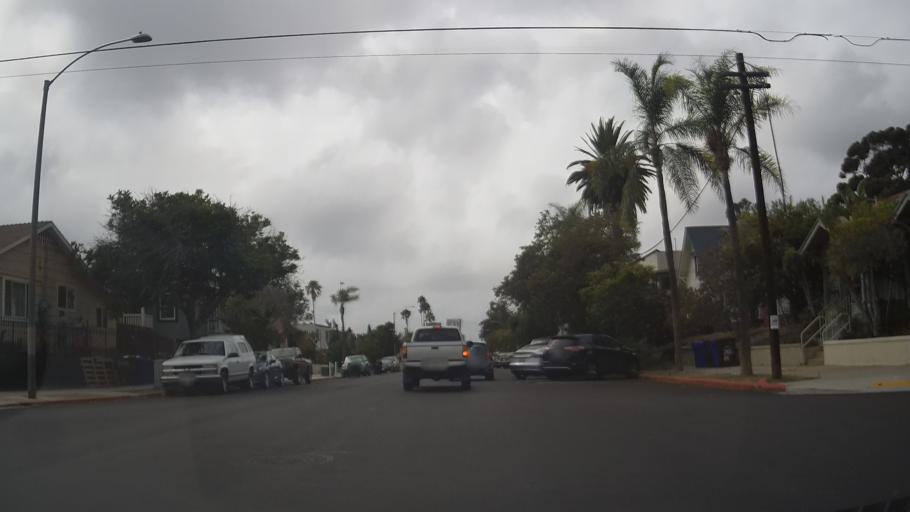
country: US
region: California
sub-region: San Diego County
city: San Diego
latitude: 32.7190
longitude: -117.1360
